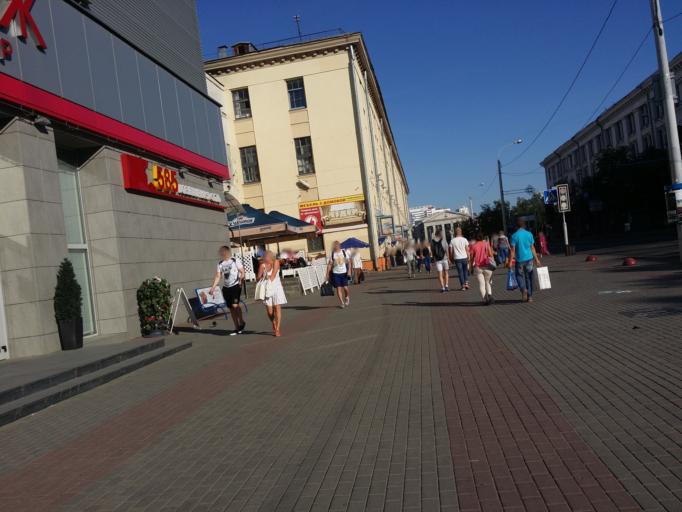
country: BY
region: Minsk
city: Minsk
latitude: 53.9172
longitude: 27.5802
